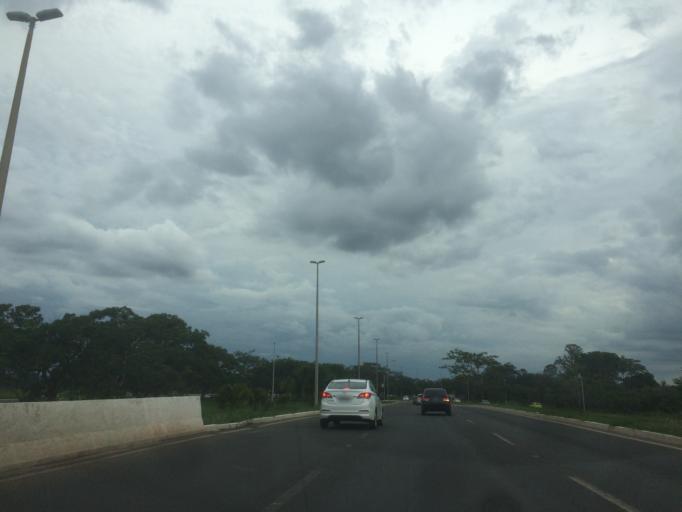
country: BR
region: Federal District
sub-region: Brasilia
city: Brasilia
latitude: -15.7965
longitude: -47.8543
